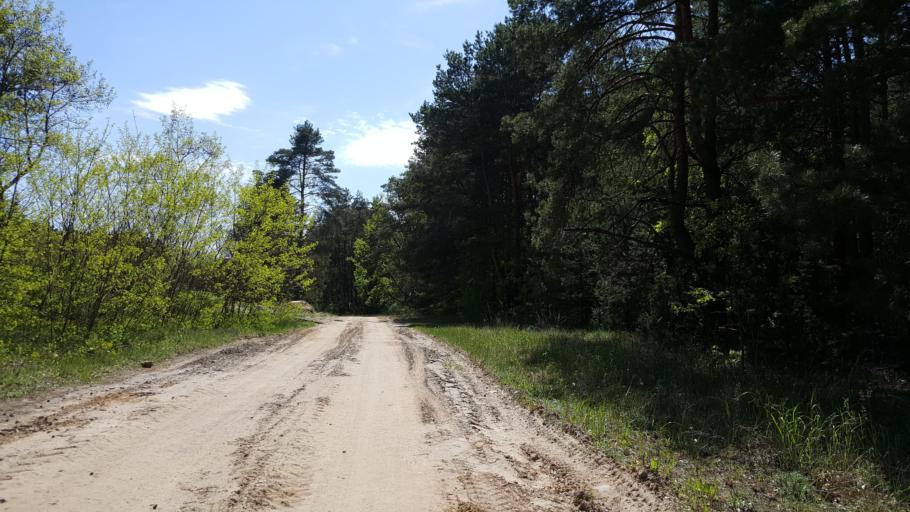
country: BY
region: Brest
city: Zhabinka
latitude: 52.3667
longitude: 24.1599
